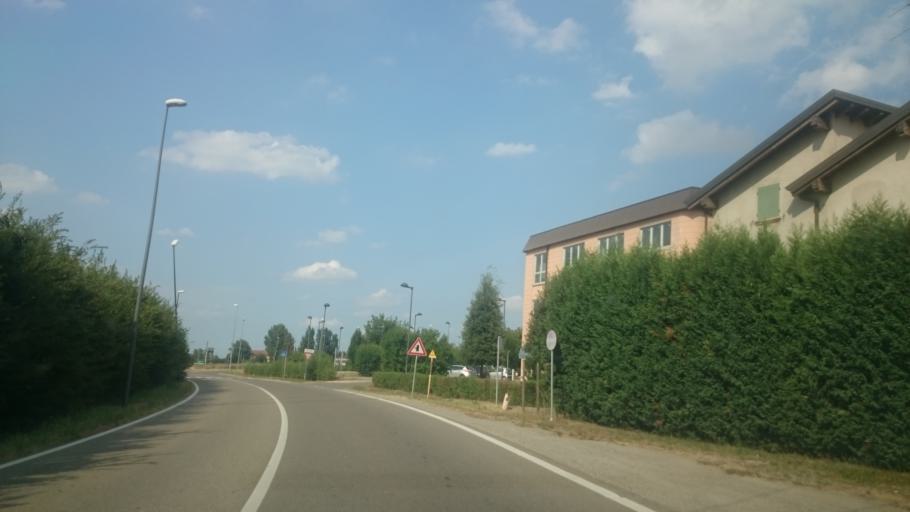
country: IT
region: Emilia-Romagna
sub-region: Provincia di Reggio Emilia
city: Salvaterra
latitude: 44.6039
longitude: 10.7746
